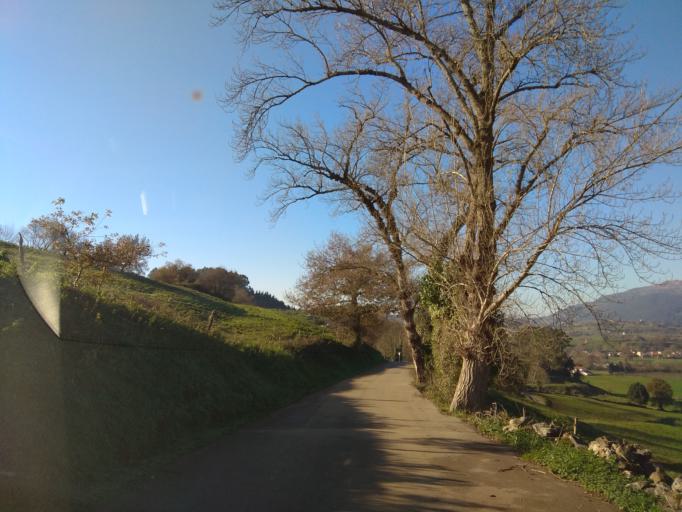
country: ES
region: Cantabria
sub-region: Provincia de Cantabria
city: Entrambasaguas
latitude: 43.3723
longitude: -3.7014
